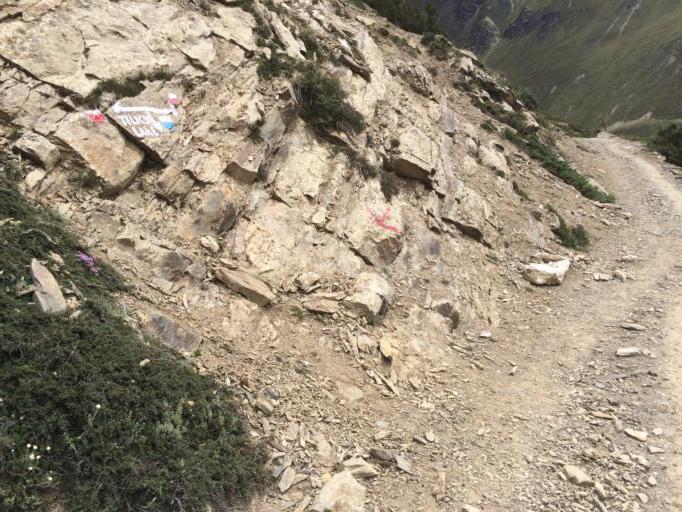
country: NP
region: Western Region
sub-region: Gandaki Zone
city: Nawal
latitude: 28.7016
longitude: 83.9847
